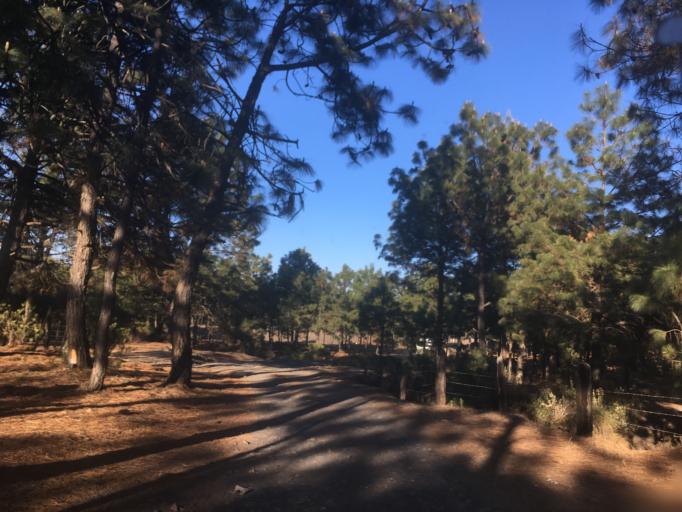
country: MX
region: Michoacan
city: Angahuan
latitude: 19.4596
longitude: -102.2364
